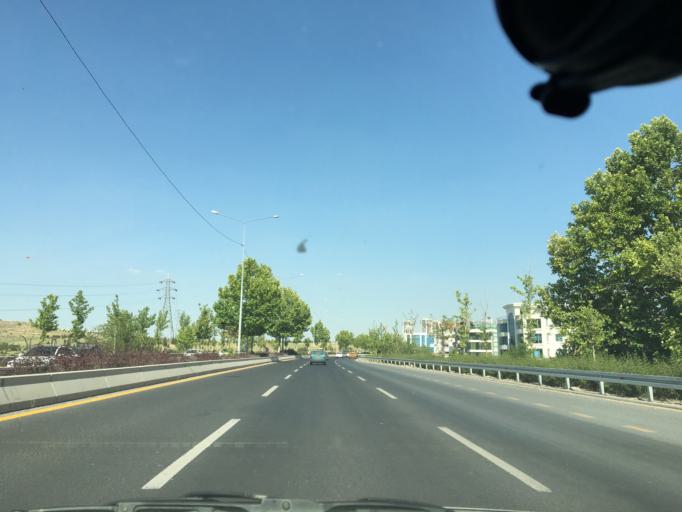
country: TR
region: Ankara
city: Batikent
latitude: 39.9166
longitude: 32.7674
